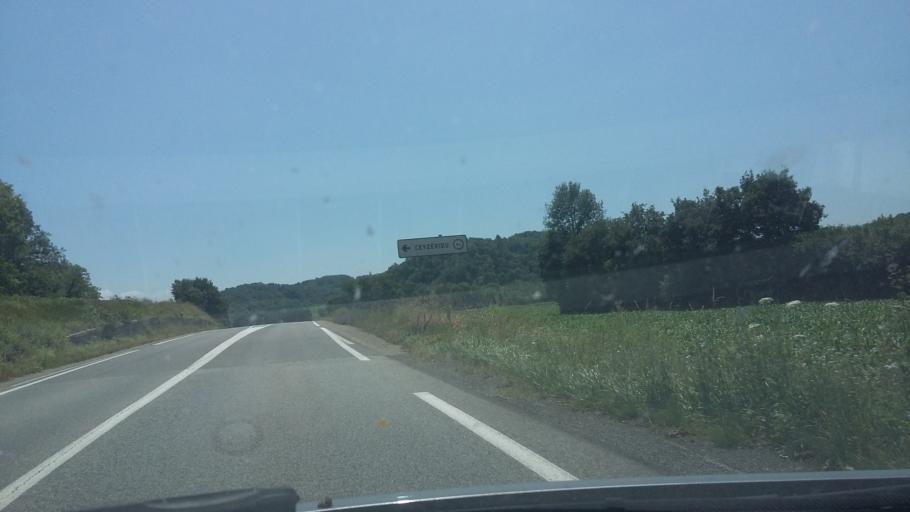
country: FR
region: Rhone-Alpes
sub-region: Departement de l'Ain
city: Belley
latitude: 45.7950
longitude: 5.6824
